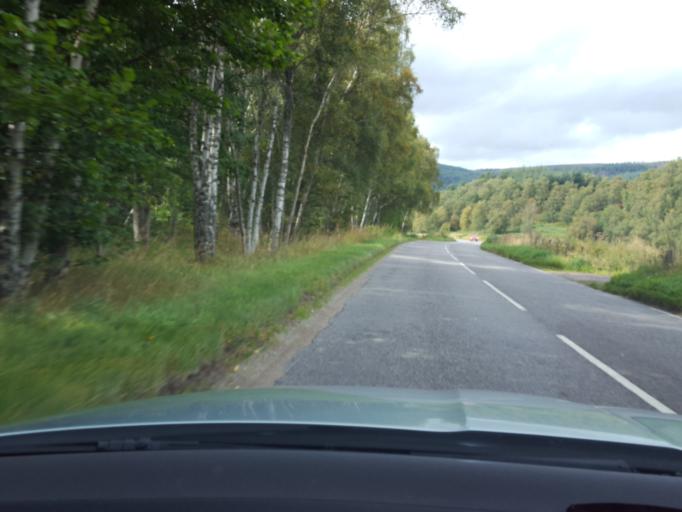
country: GB
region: Scotland
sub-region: Aberdeenshire
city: Ballater
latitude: 57.0691
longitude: -2.9628
